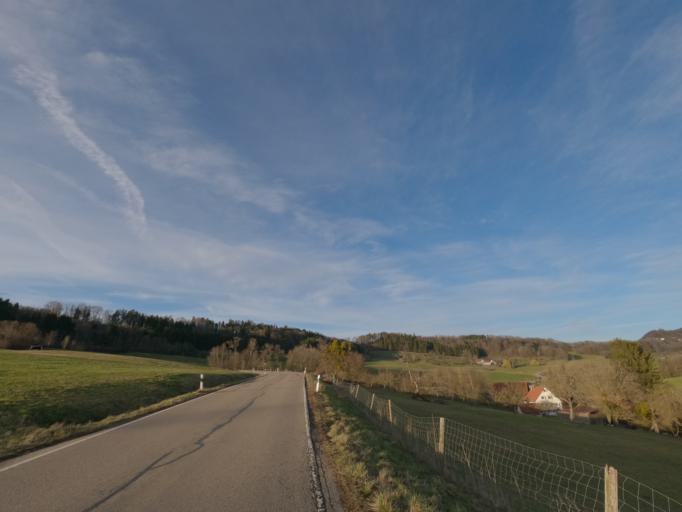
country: DE
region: Baden-Wuerttemberg
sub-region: Regierungsbezirk Stuttgart
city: Ottenbach
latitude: 48.7446
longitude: 9.7515
